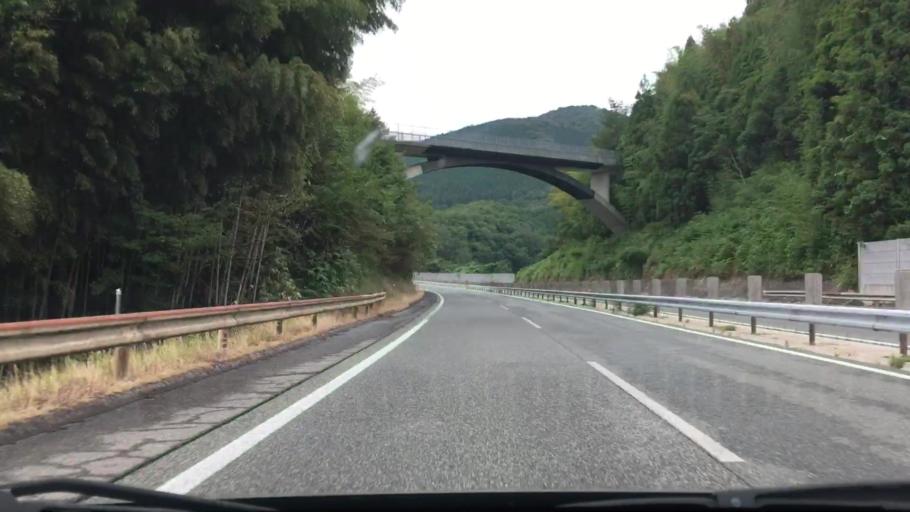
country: JP
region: Okayama
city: Niimi
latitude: 34.9627
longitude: 133.3341
